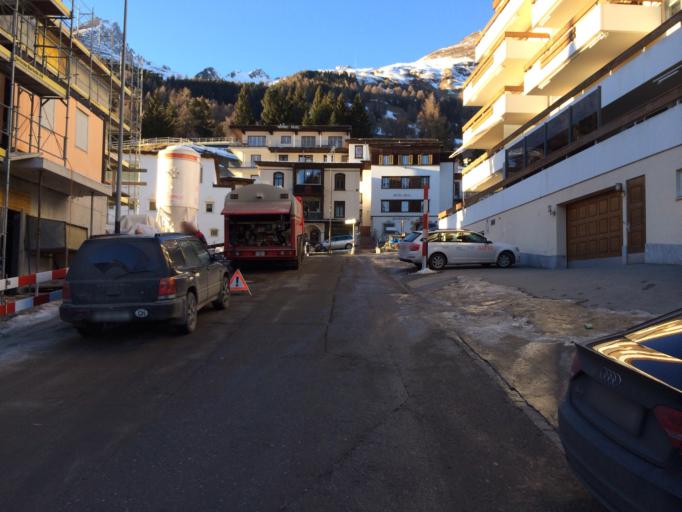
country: CH
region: Grisons
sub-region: Praettigau/Davos District
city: Davos
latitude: 46.8094
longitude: 9.8407
